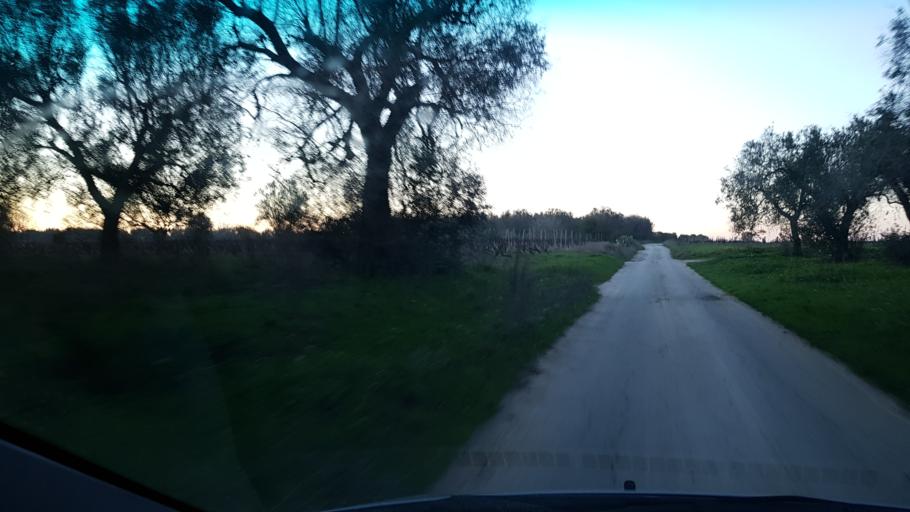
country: IT
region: Apulia
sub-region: Provincia di Brindisi
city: San Pietro Vernotico
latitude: 40.5037
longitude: 17.9772
